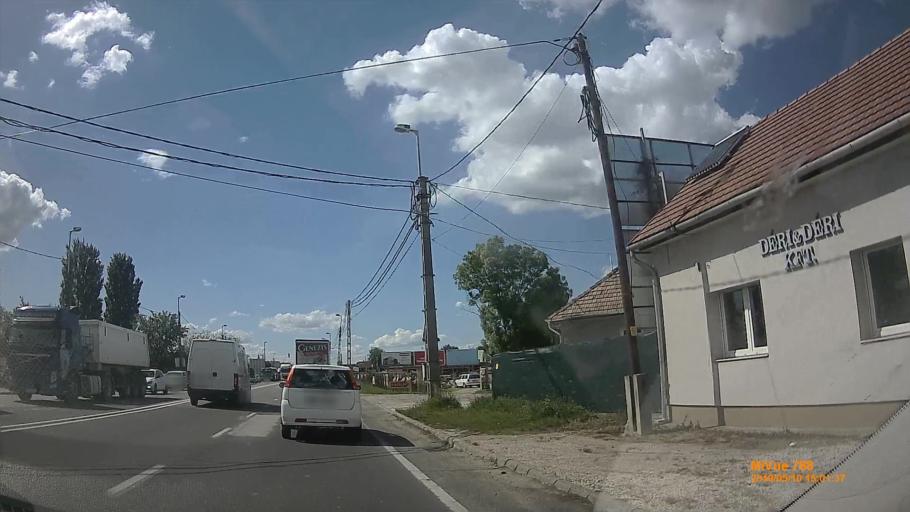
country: HU
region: Fejer
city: Szekesfehervar
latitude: 47.2059
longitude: 18.3837
